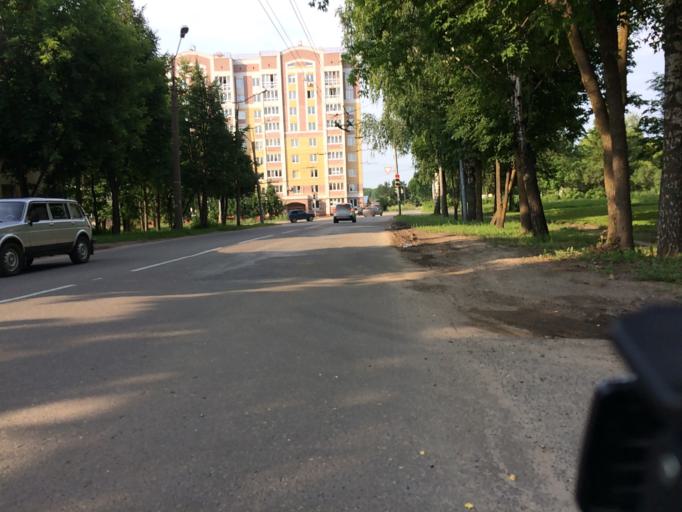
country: RU
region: Mariy-El
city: Yoshkar-Ola
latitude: 56.6309
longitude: 47.9493
